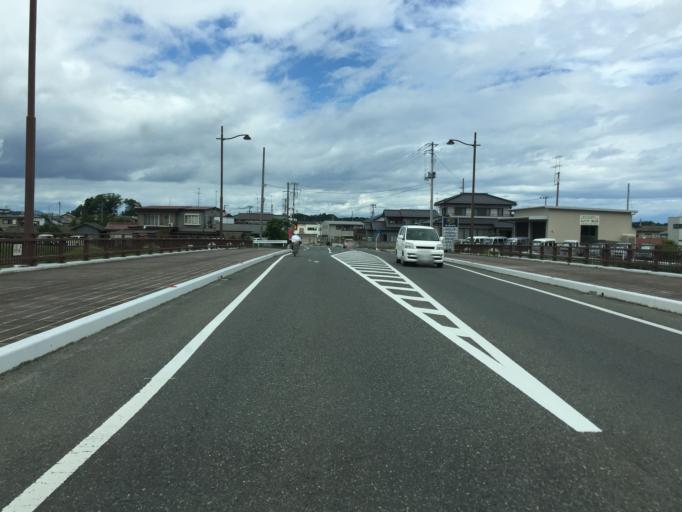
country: JP
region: Fukushima
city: Namie
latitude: 37.6981
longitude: 140.9689
